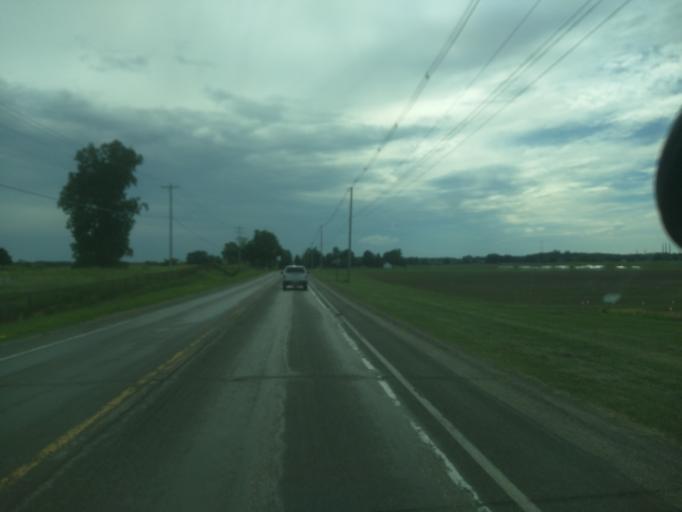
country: US
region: Michigan
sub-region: Ingham County
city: Holt
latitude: 42.6828
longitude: -84.4865
